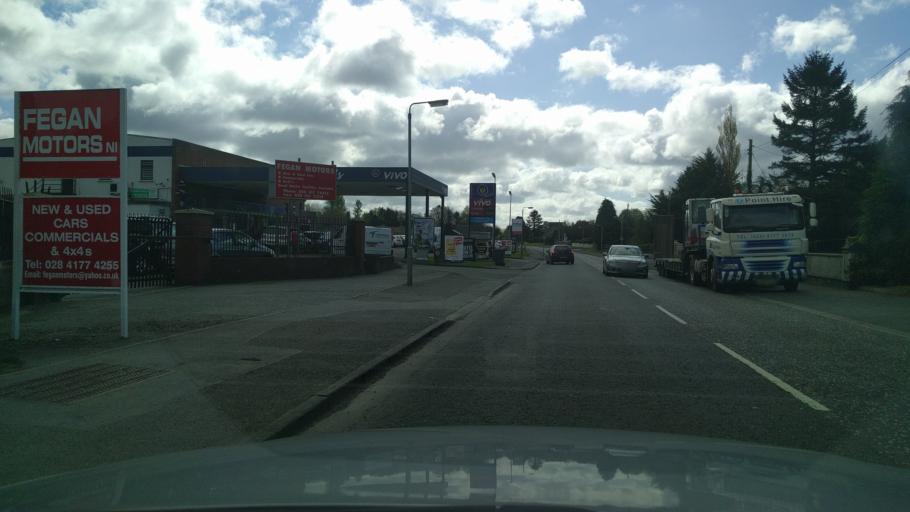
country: GB
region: Northern Ireland
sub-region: Down District
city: Warrenpoint
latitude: 54.1135
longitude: -6.2609
